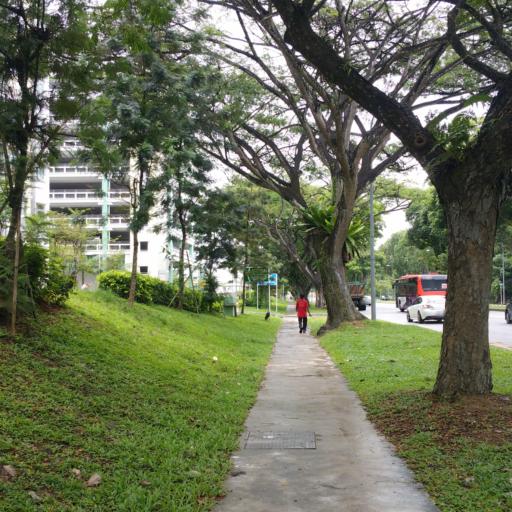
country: MY
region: Johor
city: Kampung Pasir Gudang Baru
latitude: 1.4193
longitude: 103.8472
